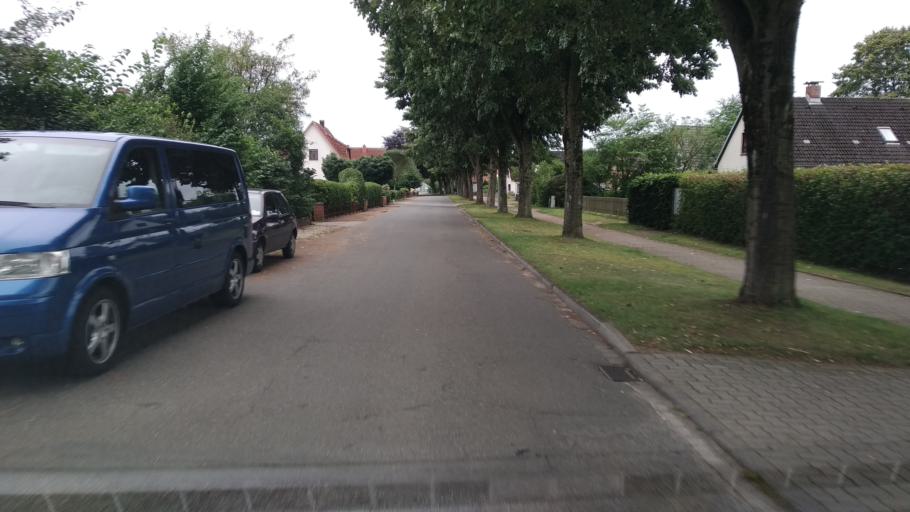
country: DE
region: Schleswig-Holstein
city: Schuby
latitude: 54.5233
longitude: 9.4820
